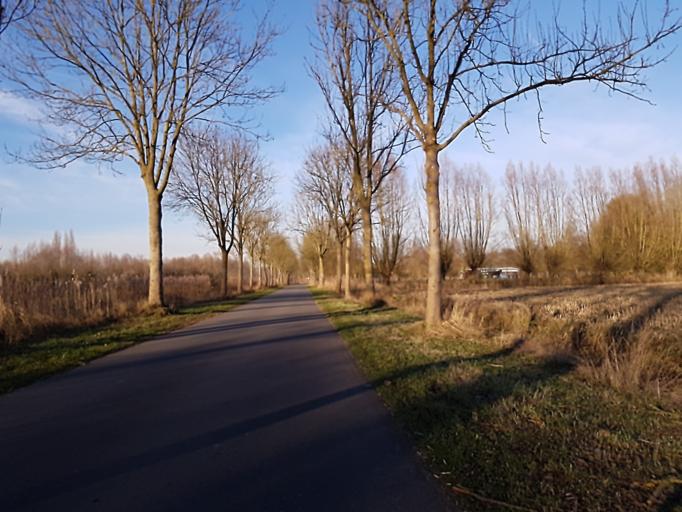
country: BE
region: Flanders
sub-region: Provincie Antwerpen
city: Puurs
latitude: 51.1096
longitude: 4.2864
